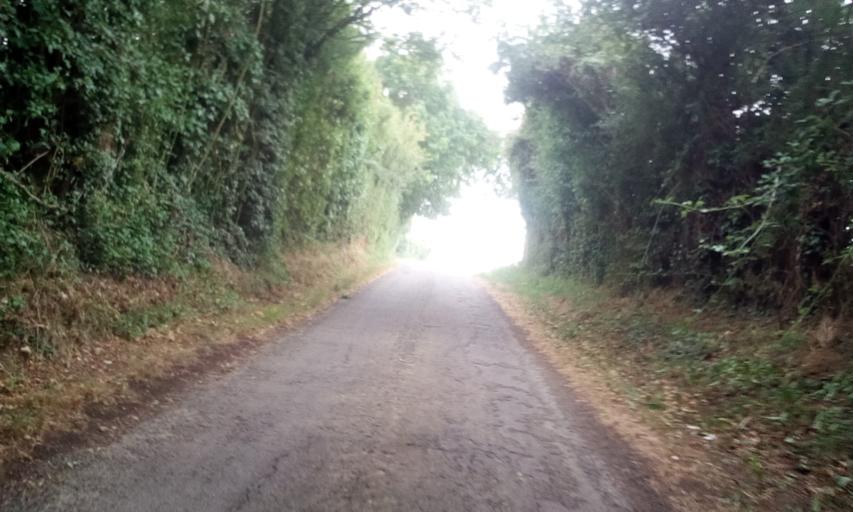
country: FR
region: Lower Normandy
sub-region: Departement du Calvados
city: Thury-Harcourt
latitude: 49.0043
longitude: -0.4413
